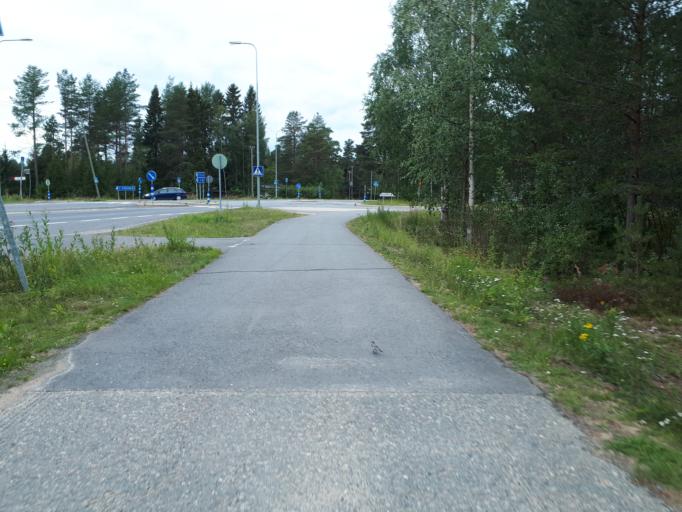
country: FI
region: Northern Ostrobothnia
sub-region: Oulunkaari
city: Ii
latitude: 65.3164
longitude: 25.3888
